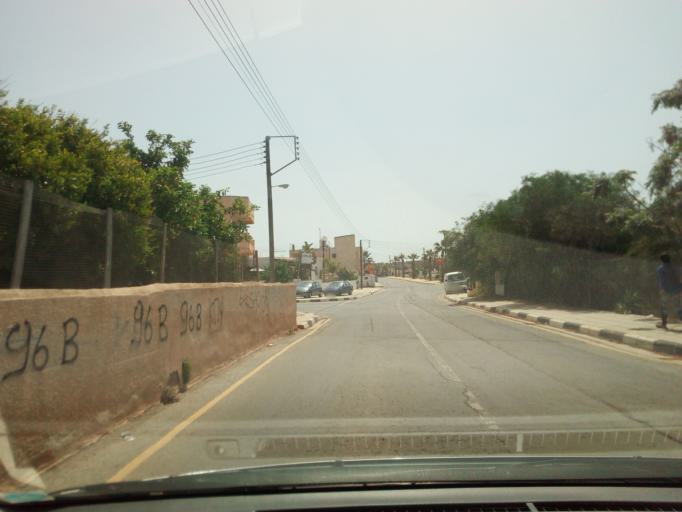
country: CY
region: Larnaka
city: Xylotymbou
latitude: 34.9918
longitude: 33.7845
